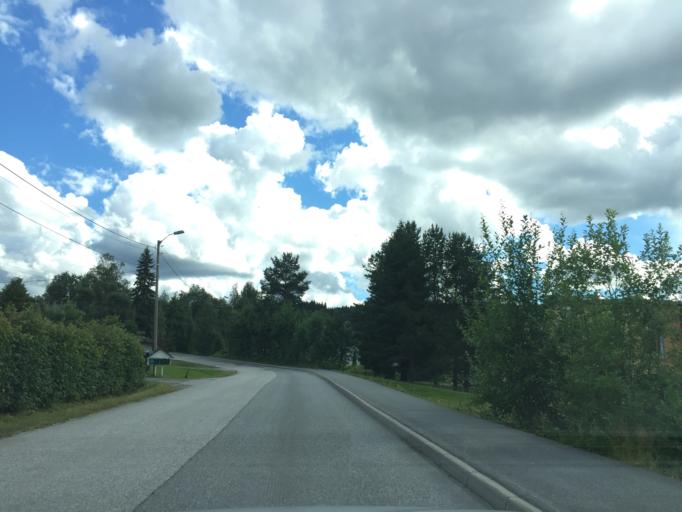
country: NO
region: Hedmark
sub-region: Kongsvinger
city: Kongsvinger
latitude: 60.1834
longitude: 12.0105
